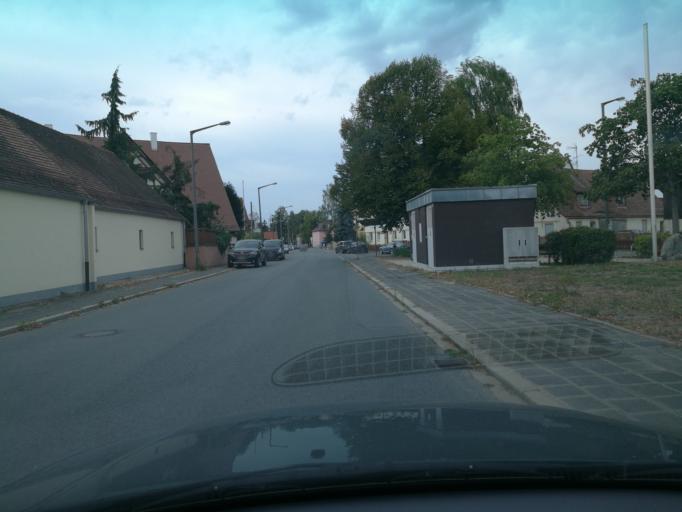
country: DE
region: Bavaria
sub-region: Regierungsbezirk Mittelfranken
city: Wetzendorf
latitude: 49.4699
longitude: 11.0418
